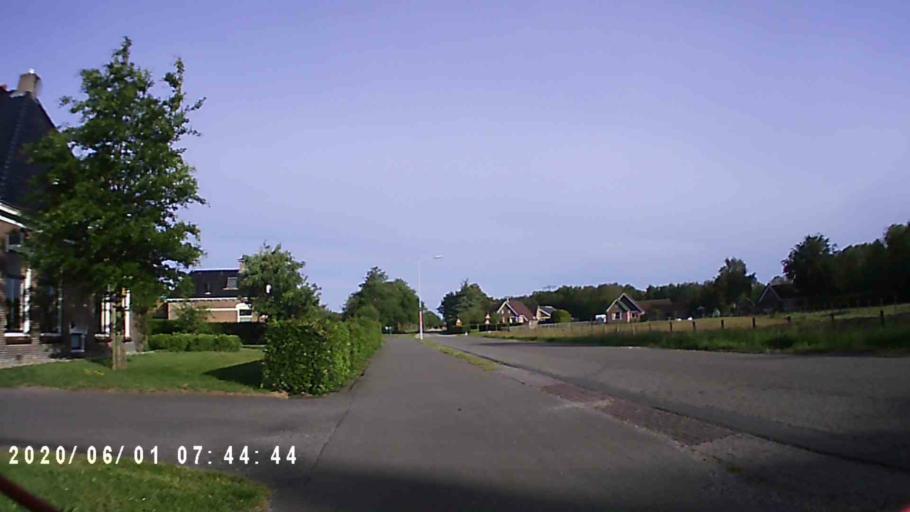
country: NL
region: Friesland
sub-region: Gemeente Dantumadiel
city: Rinsumageast
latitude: 53.2918
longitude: 5.9661
